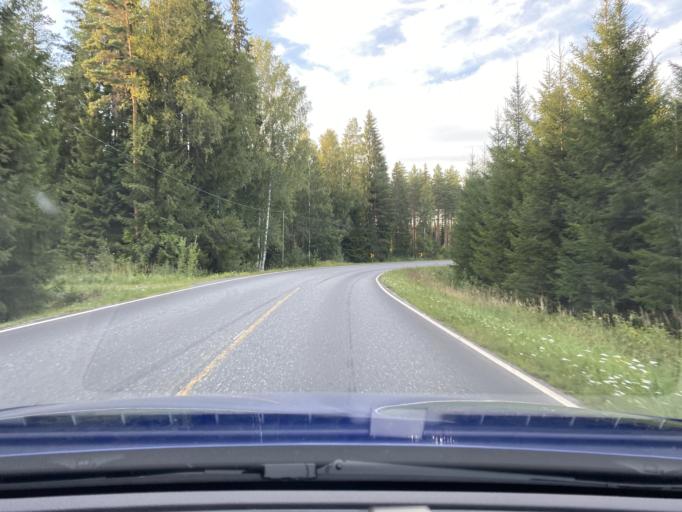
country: FI
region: Pirkanmaa
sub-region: Lounais-Pirkanmaa
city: Punkalaidun
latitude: 61.1638
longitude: 23.0597
